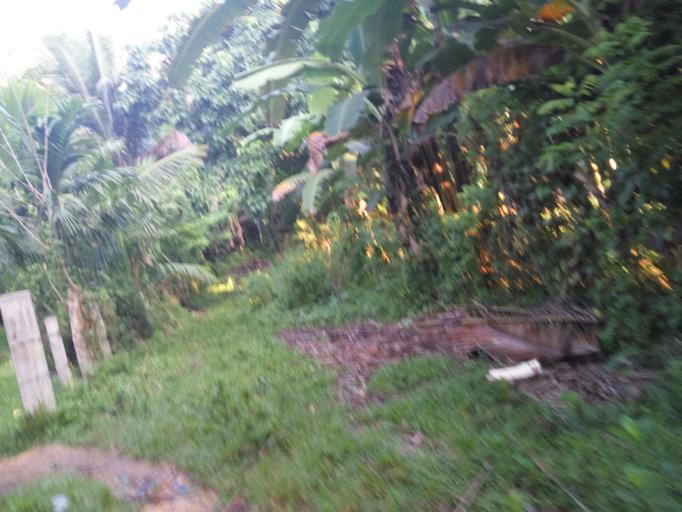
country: PH
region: Central Luzon
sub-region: Province of Aurora
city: Maria Aurora
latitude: 15.8894
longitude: 121.5449
